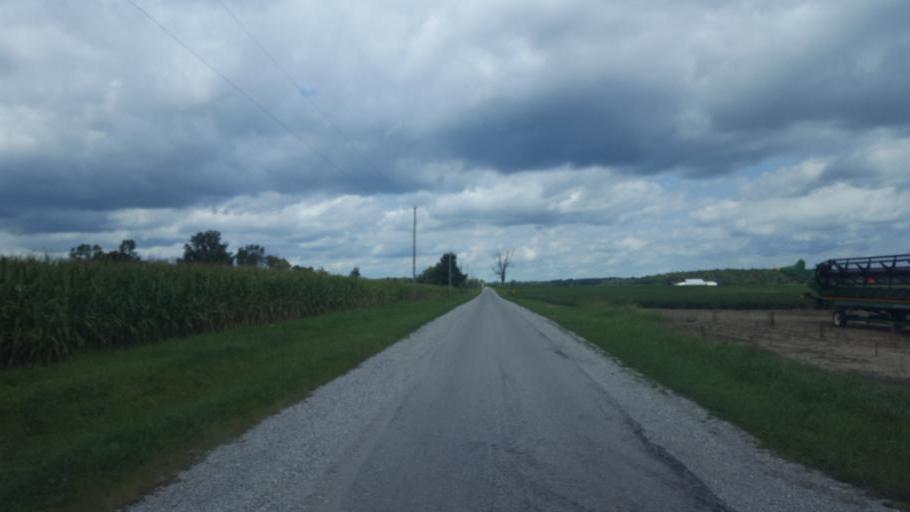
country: US
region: Ohio
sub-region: Huron County
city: Willard
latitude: 41.0999
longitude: -82.8423
